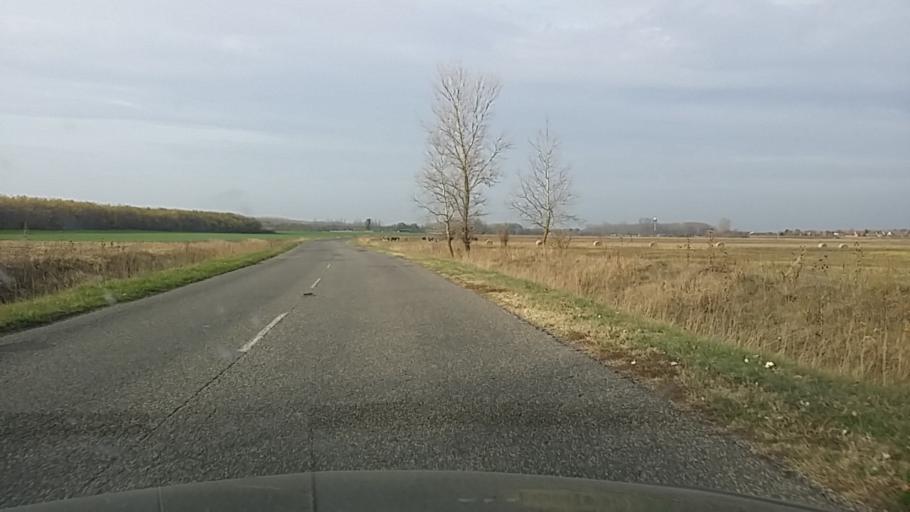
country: HU
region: Szabolcs-Szatmar-Bereg
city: Nyirbogdany
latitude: 48.0479
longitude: 21.8635
